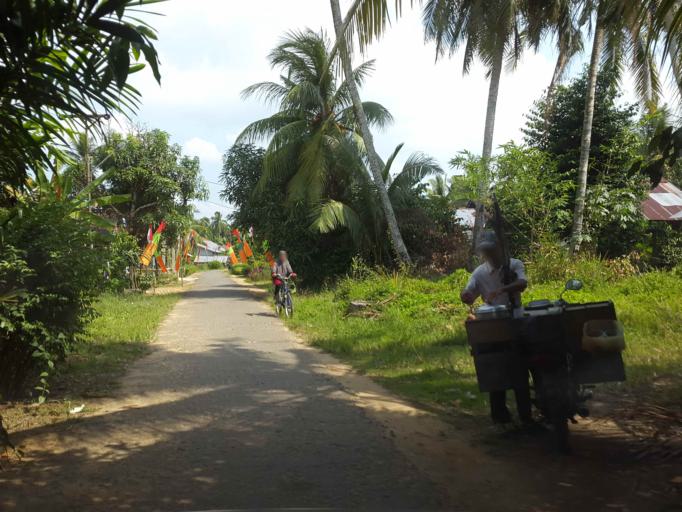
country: ID
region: West Kalimantan
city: Pemangkat
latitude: 1.7702
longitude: 109.3217
